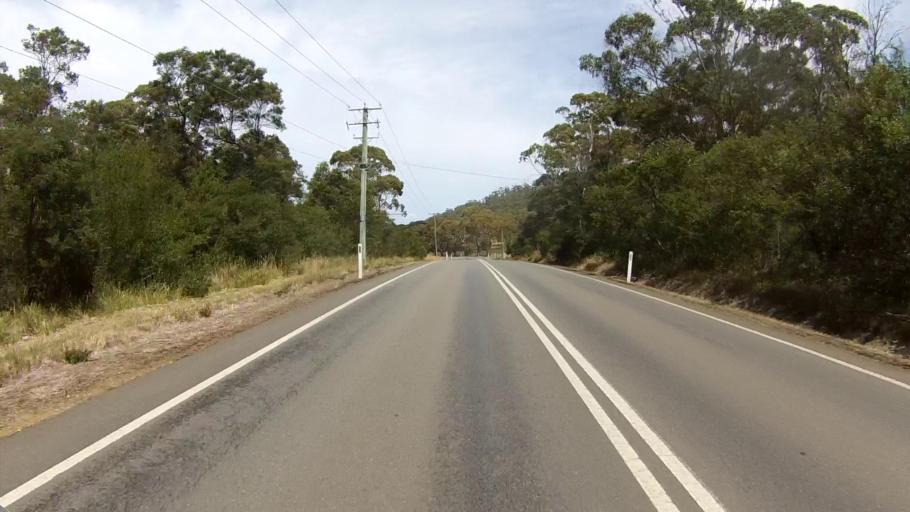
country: AU
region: Tasmania
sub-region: Clarence
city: Sandford
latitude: -43.0148
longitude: 147.4903
